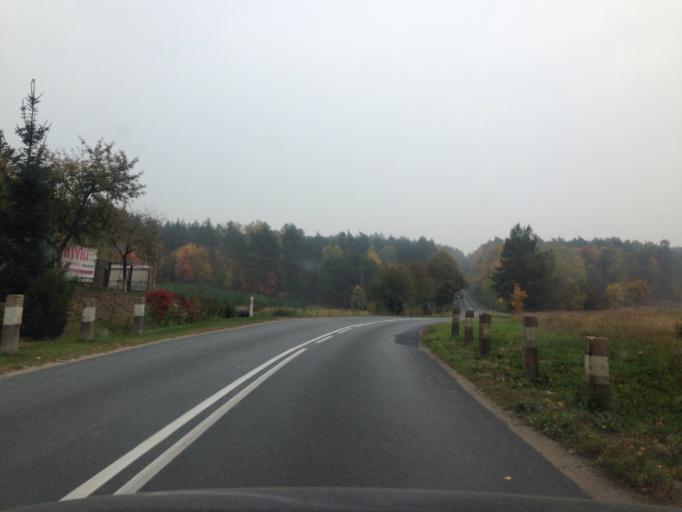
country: PL
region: Kujawsko-Pomorskie
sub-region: Powiat brodnicki
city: Gorzno
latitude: 53.2434
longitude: 19.6775
